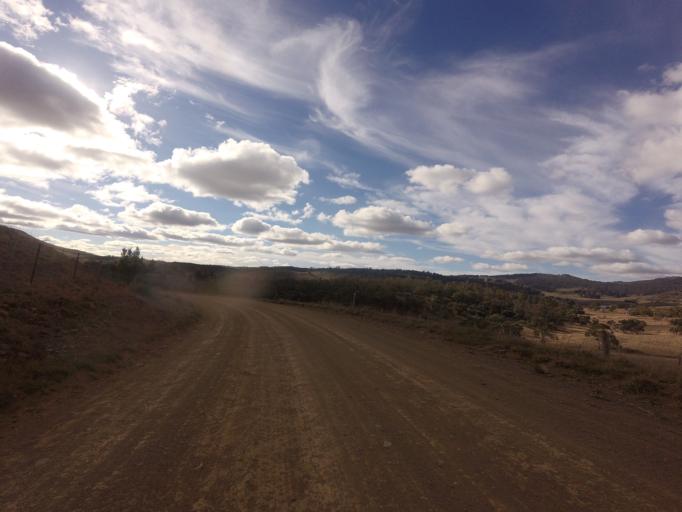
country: AU
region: Tasmania
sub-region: Brighton
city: Bridgewater
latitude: -42.4513
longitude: 147.2420
